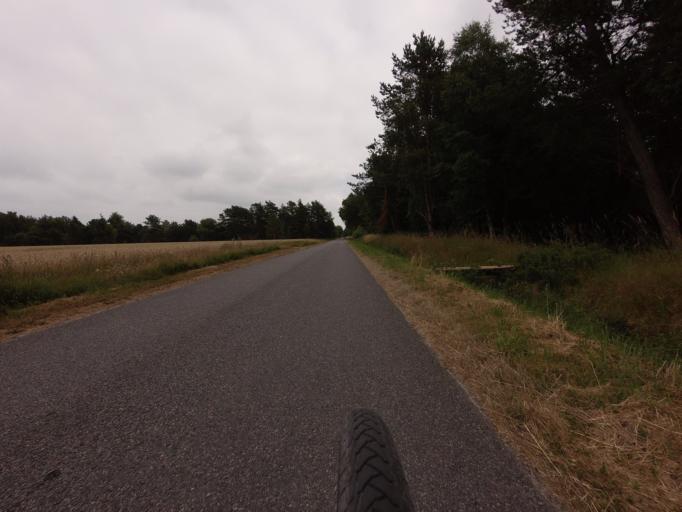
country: DK
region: North Denmark
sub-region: Laeso Kommune
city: Byrum
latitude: 57.2921
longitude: 10.9528
